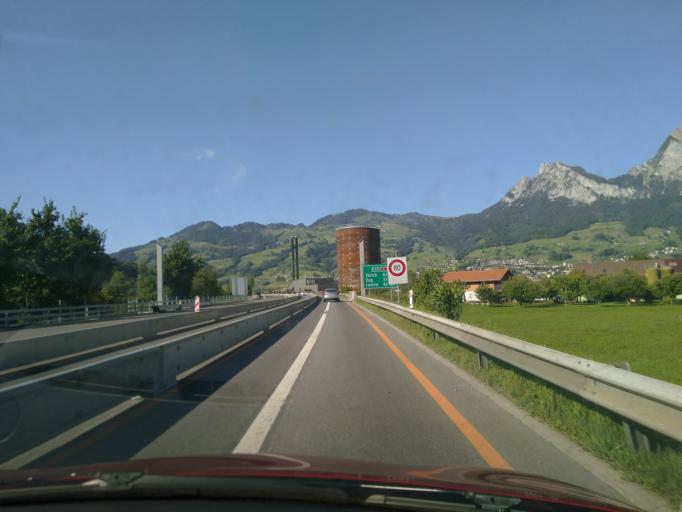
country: CH
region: Schwyz
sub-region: Bezirk Schwyz
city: Ingenbohl
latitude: 47.0106
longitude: 8.6238
